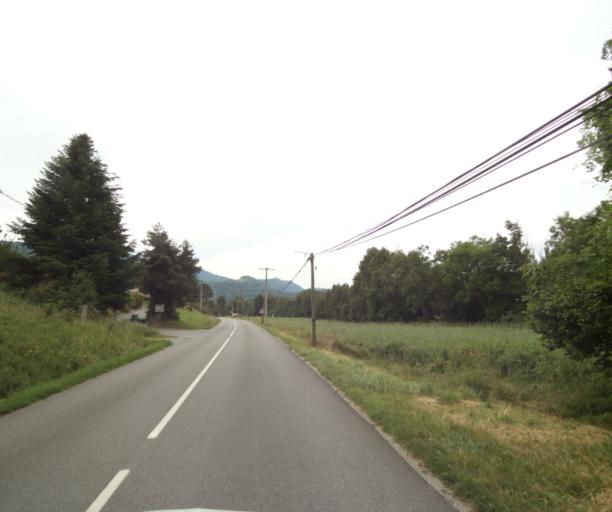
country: FR
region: Rhone-Alpes
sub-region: Departement de la Haute-Savoie
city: Allinges
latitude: 46.3256
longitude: 6.4743
